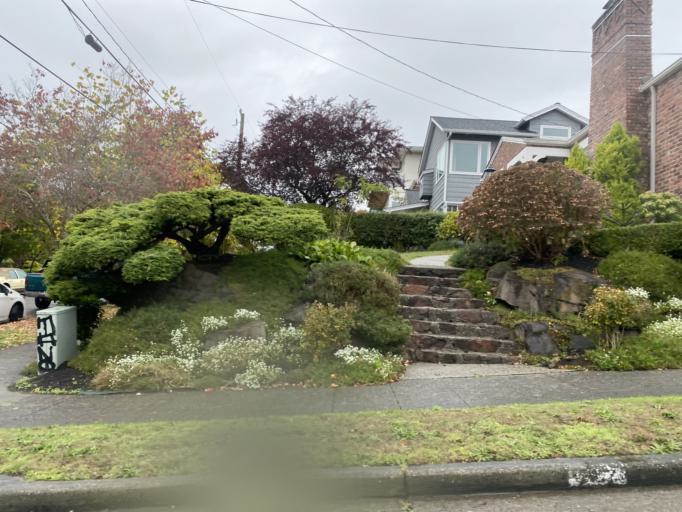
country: US
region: Washington
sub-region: King County
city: Seattle
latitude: 47.6446
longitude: -122.3942
